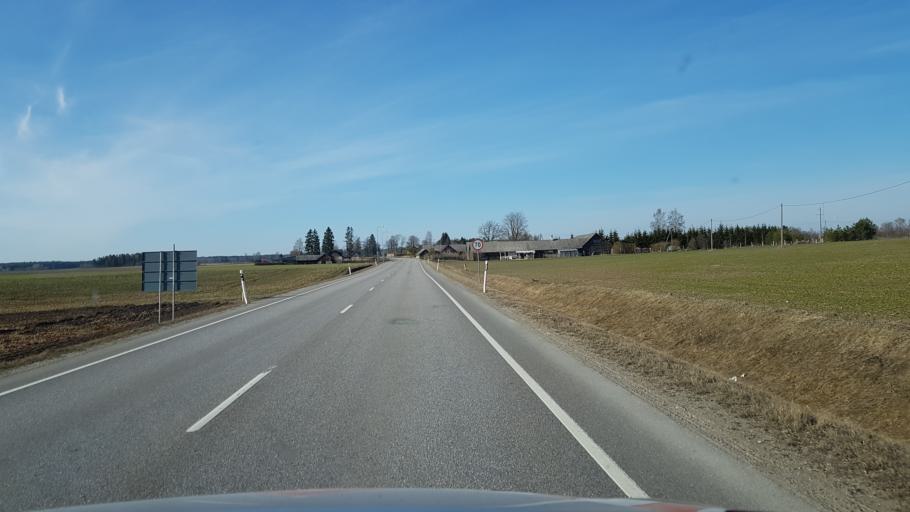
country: EE
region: Laeaene-Virumaa
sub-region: Vinni vald
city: Vinni
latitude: 59.1441
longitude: 26.5958
